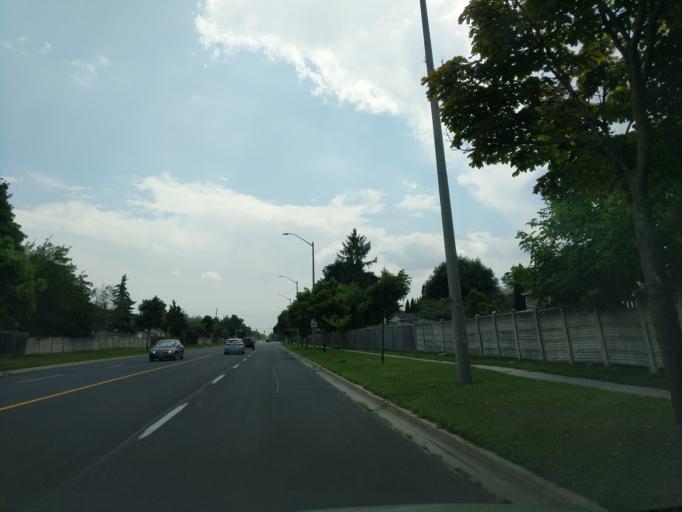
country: CA
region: Ontario
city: Markham
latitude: 43.8237
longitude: -79.3180
